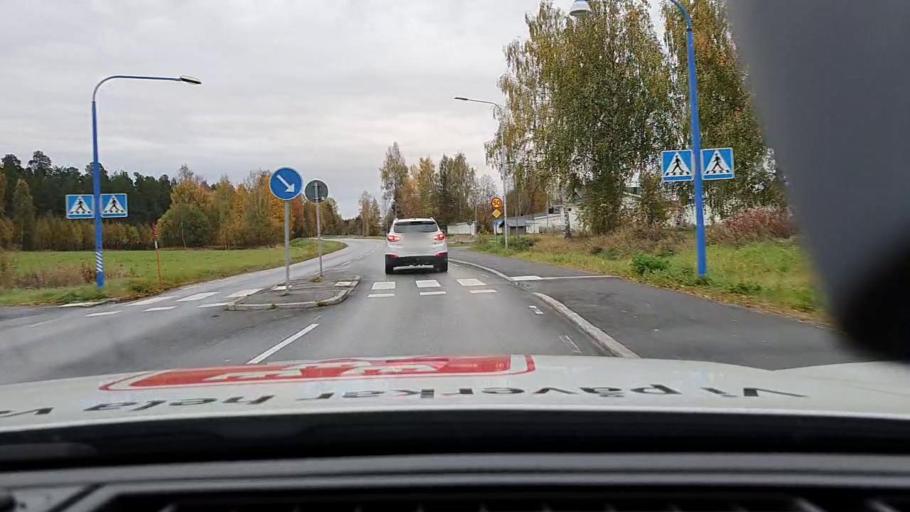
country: SE
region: Norrbotten
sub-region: Bodens Kommun
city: Saevast
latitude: 65.7716
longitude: 21.7016
